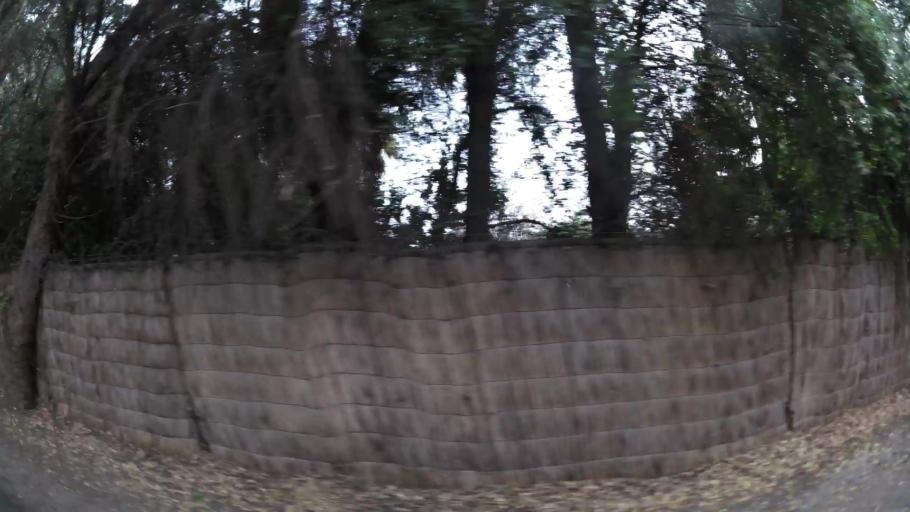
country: CL
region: Santiago Metropolitan
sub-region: Provincia de Chacabuco
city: Chicureo Abajo
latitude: -33.2689
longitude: -70.7051
